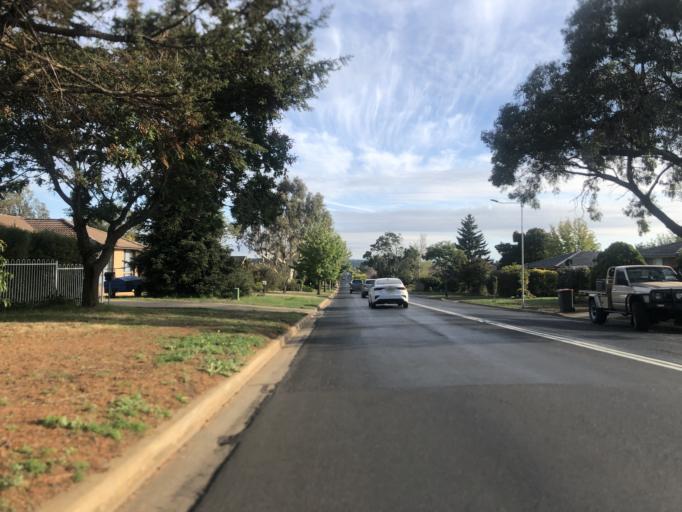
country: AU
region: New South Wales
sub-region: Orange Municipality
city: Orange
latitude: -33.3047
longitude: 149.0944
